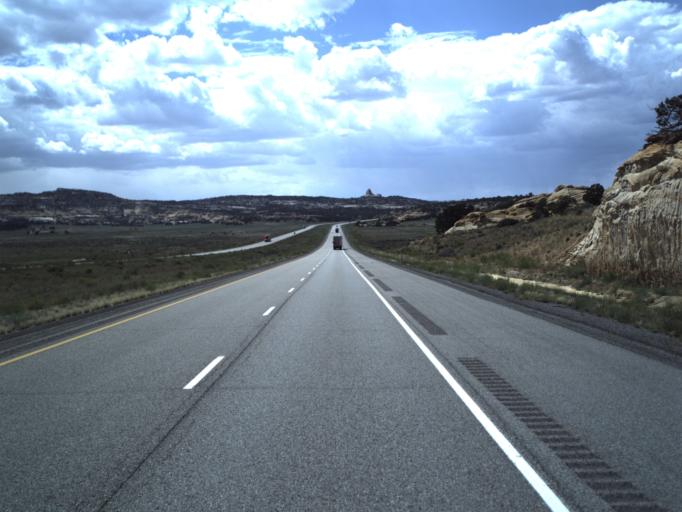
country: US
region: Utah
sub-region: Emery County
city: Castle Dale
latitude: 38.8692
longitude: -110.7756
